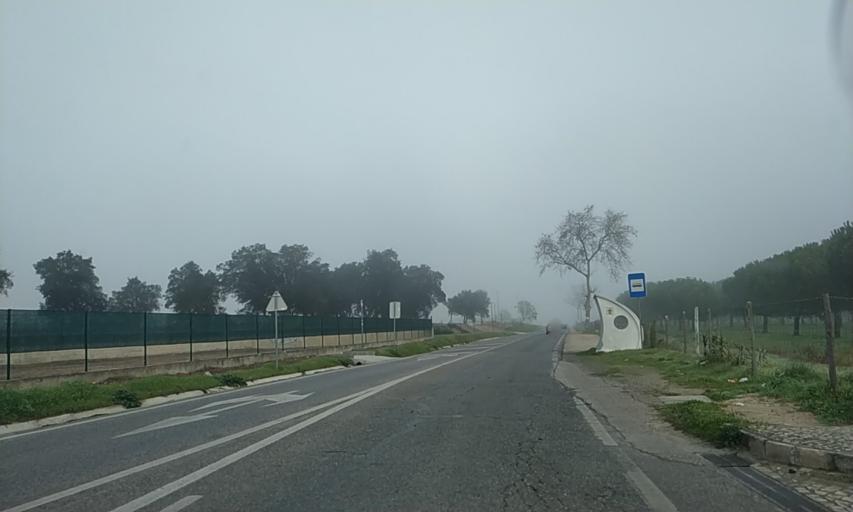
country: PT
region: Setubal
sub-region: Palmela
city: Pinhal Novo
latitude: 38.6410
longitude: -8.9147
